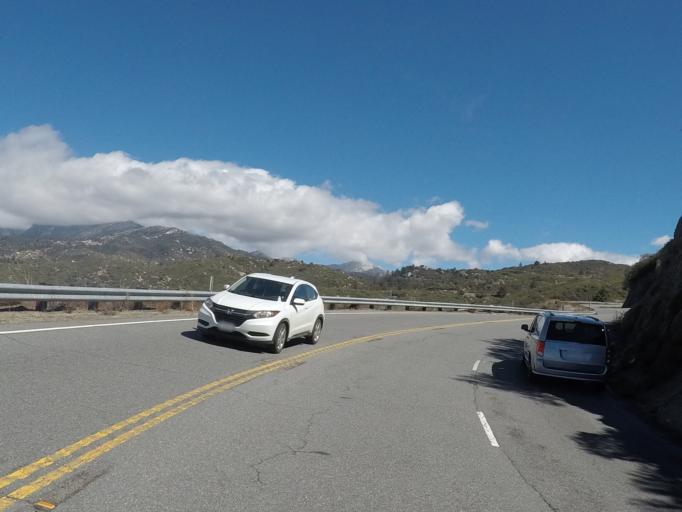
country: US
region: California
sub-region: Riverside County
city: Idyllwild
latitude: 33.7020
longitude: -116.7470
